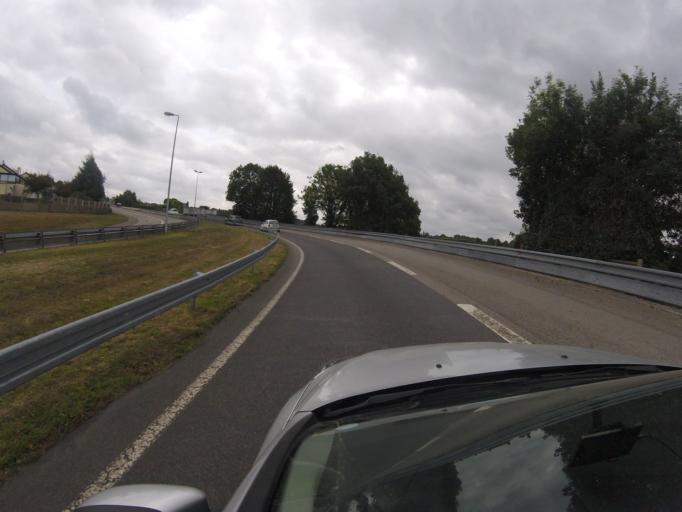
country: FR
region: Lower Normandy
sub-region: Departement de la Manche
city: Cherbourg-Octeville
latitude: 49.6215
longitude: -1.6155
